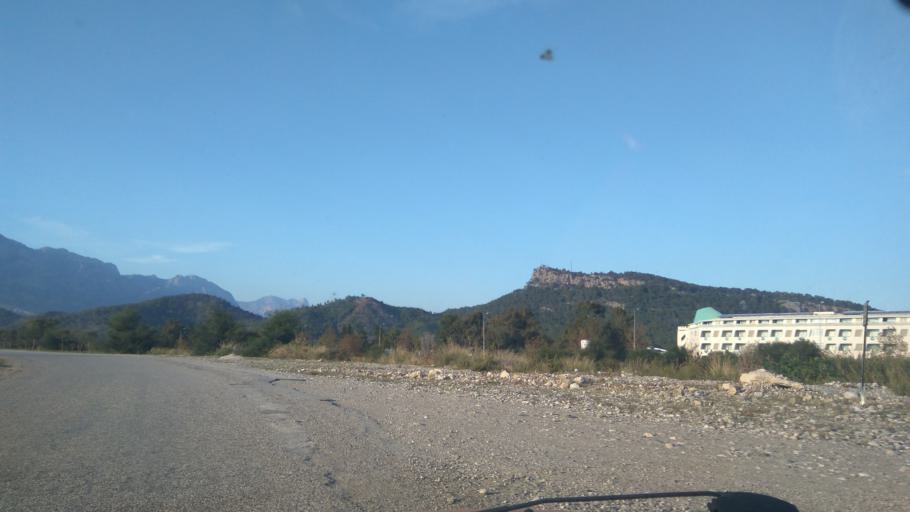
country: TR
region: Antalya
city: Kemer
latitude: 36.5645
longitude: 30.5712
